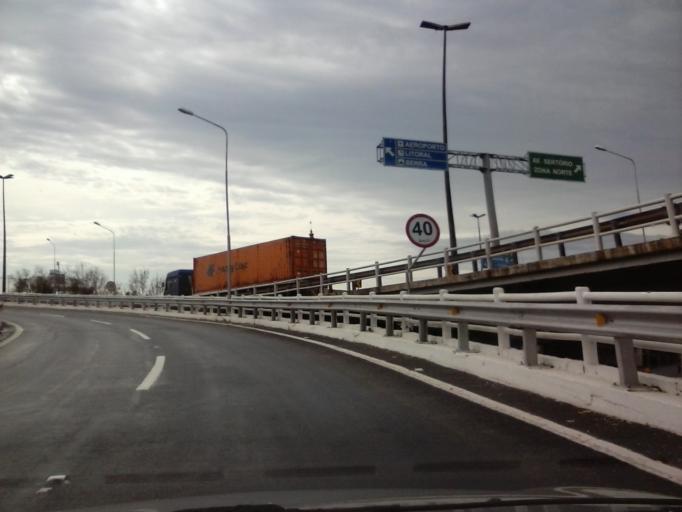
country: BR
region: Rio Grande do Sul
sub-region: Porto Alegre
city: Porto Alegre
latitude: -29.9988
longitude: -51.2058
